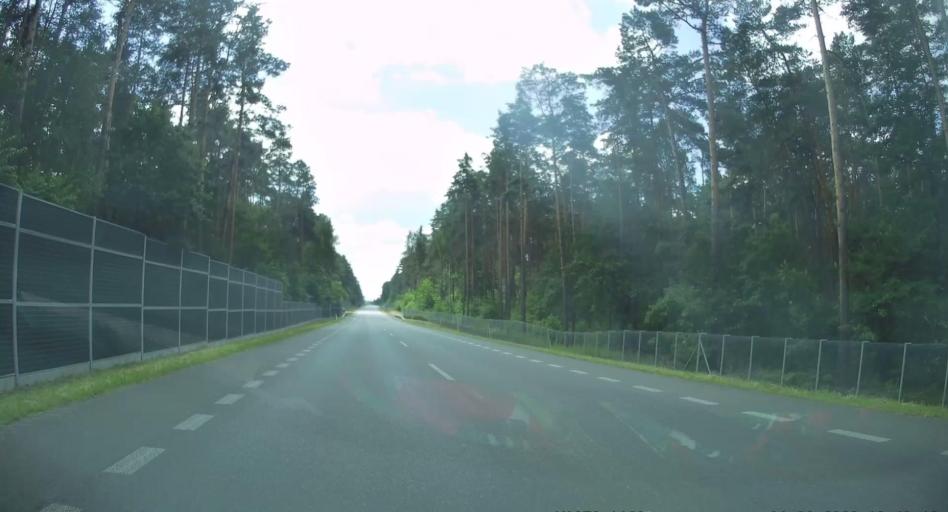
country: PL
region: Subcarpathian Voivodeship
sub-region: Powiat mielecki
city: Mielec
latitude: 50.2708
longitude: 21.4956
